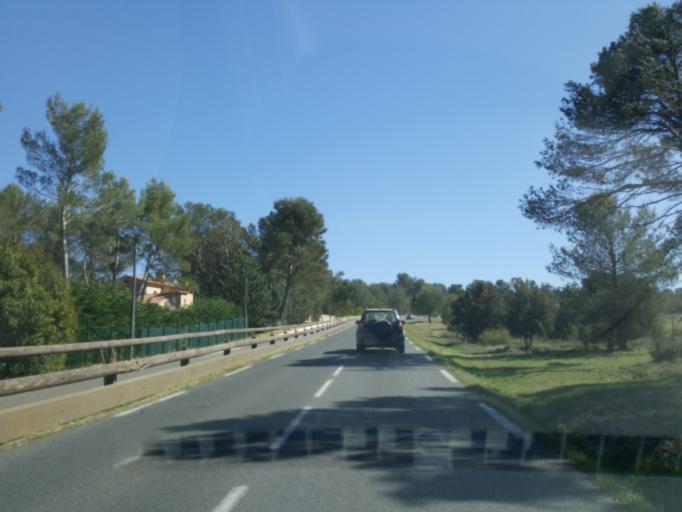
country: FR
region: Provence-Alpes-Cote d'Azur
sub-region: Departement des Bouches-du-Rhone
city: Cabries
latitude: 43.4509
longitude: 5.3598
